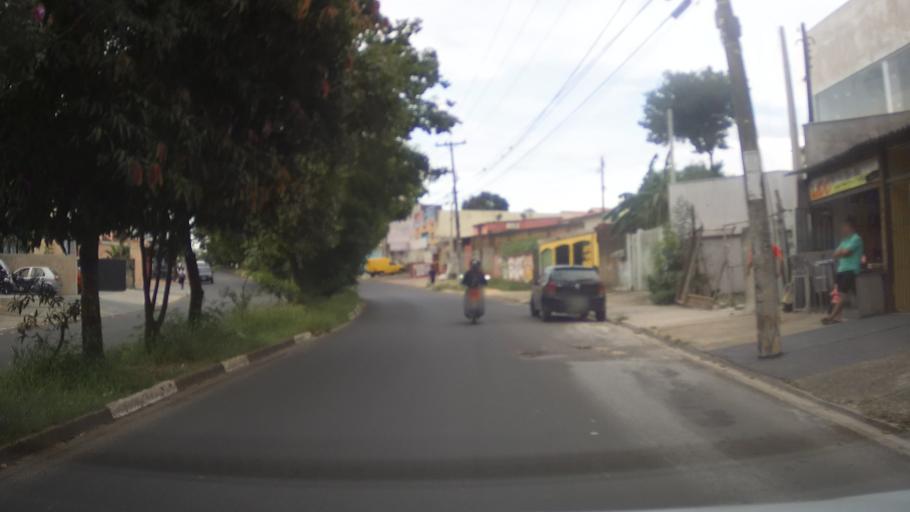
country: BR
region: Sao Paulo
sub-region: Hortolandia
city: Hortolandia
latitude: -22.9530
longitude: -47.1849
